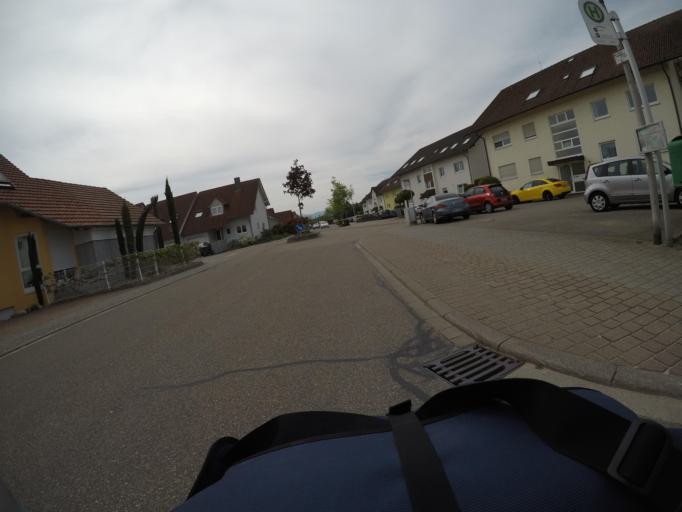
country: DE
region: Baden-Wuerttemberg
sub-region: Karlsruhe Region
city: Hugelsheim
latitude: 48.7933
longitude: 8.1096
